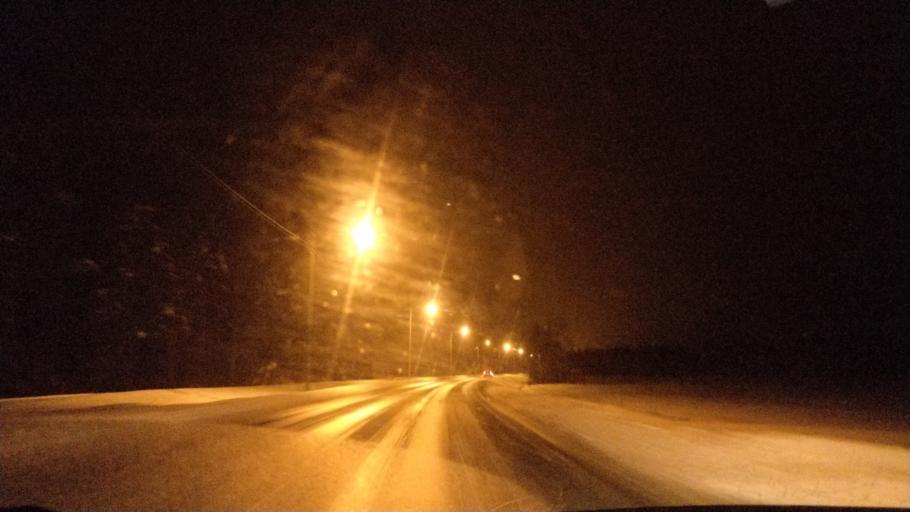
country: FI
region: Lapland
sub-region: Rovaniemi
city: Rovaniemi
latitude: 66.2602
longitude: 25.3425
